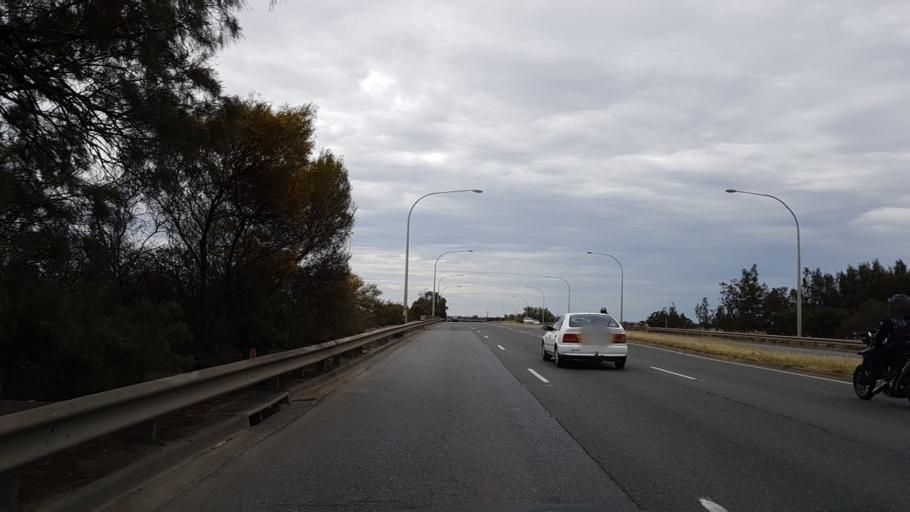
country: AU
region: South Australia
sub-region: Port Adelaide Enfield
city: Enfield
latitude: -34.8206
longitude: 138.5980
